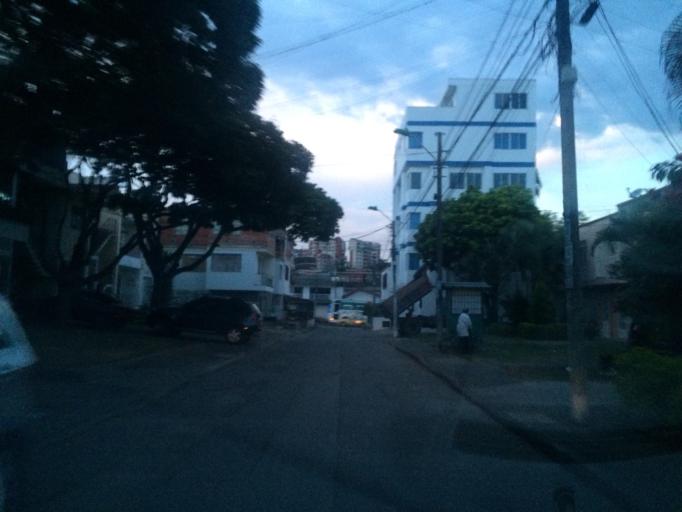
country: CO
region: Valle del Cauca
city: Cali
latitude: 3.4241
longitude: -76.5493
